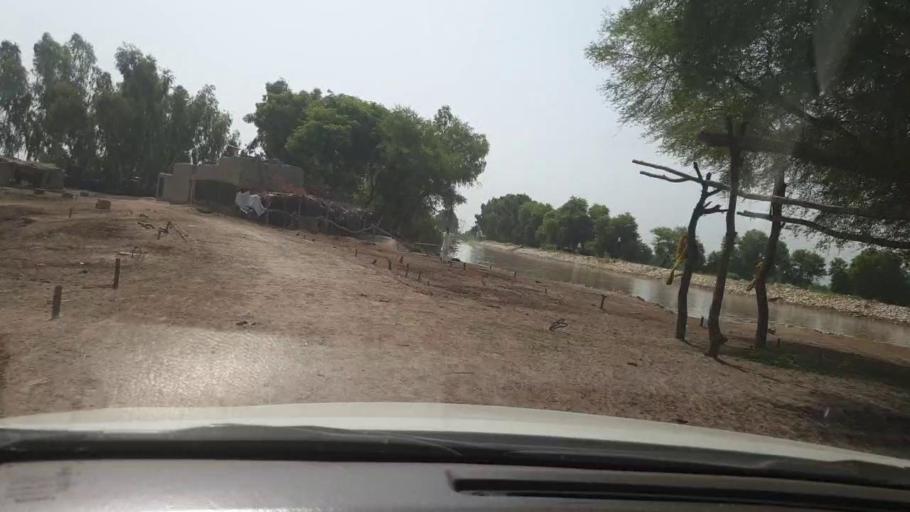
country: PK
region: Sindh
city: Rustam jo Goth
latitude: 27.9727
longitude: 68.7791
